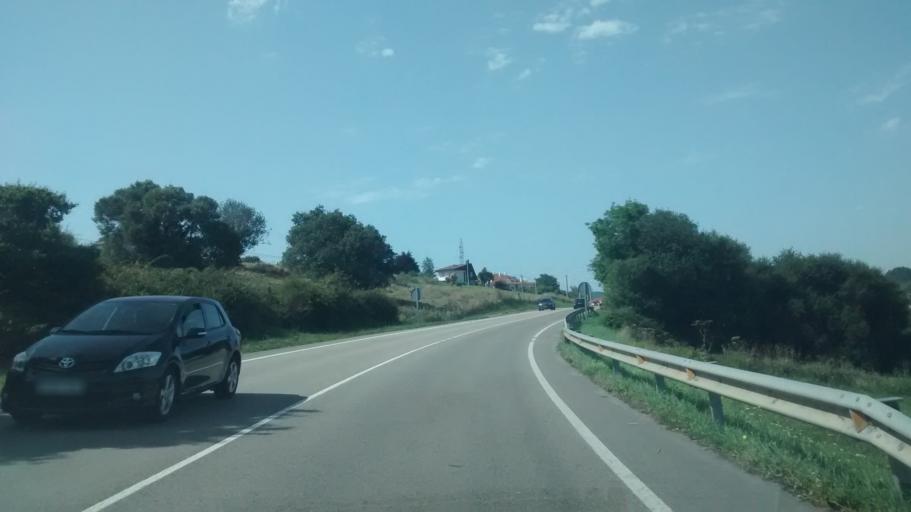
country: ES
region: Cantabria
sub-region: Provincia de Cantabria
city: Arnuero
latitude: 43.4484
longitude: -3.5601
